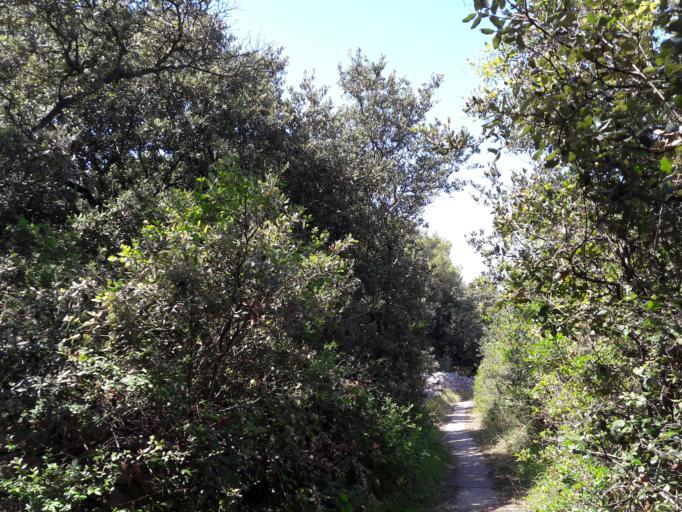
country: HR
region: Licko-Senjska
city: Novalja
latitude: 44.3671
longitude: 14.6944
